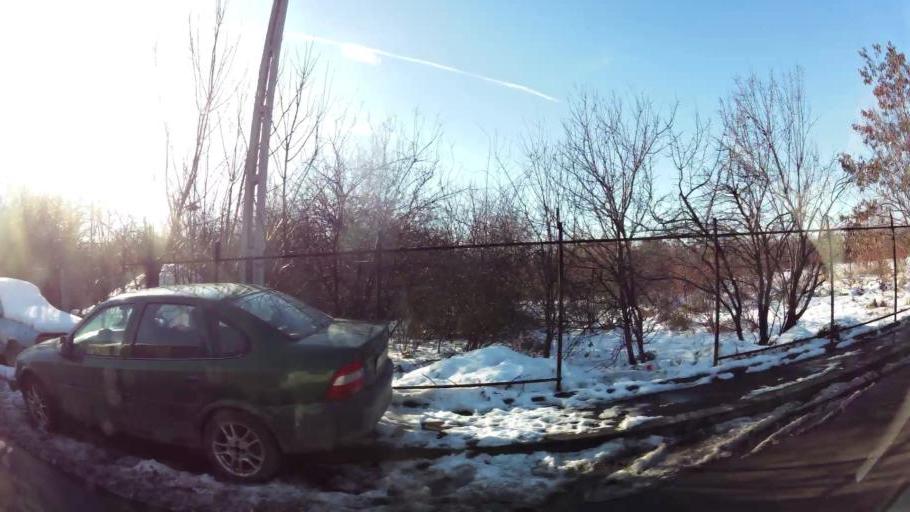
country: RO
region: Ilfov
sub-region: Comuna Fundeni-Dobroesti
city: Fundeni
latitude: 44.4781
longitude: 26.1436
